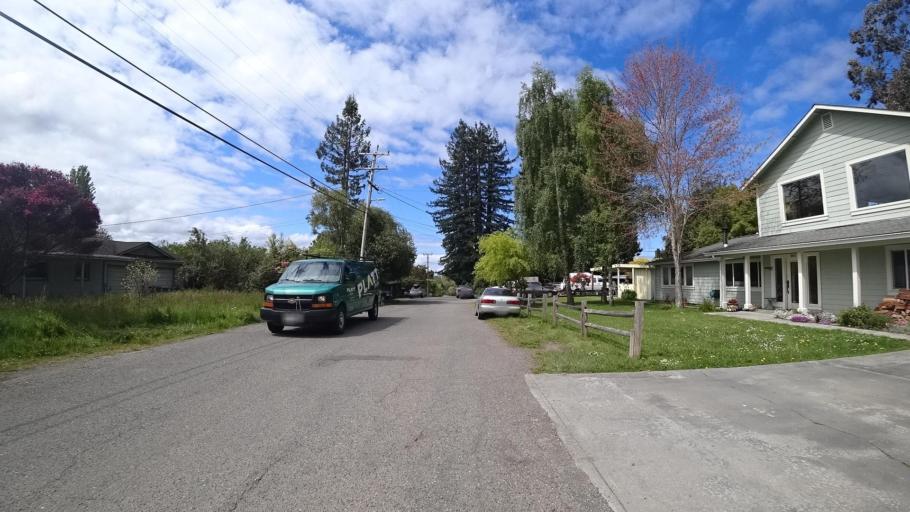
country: US
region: California
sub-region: Humboldt County
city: Bayside
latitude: 40.8465
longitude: -124.0639
